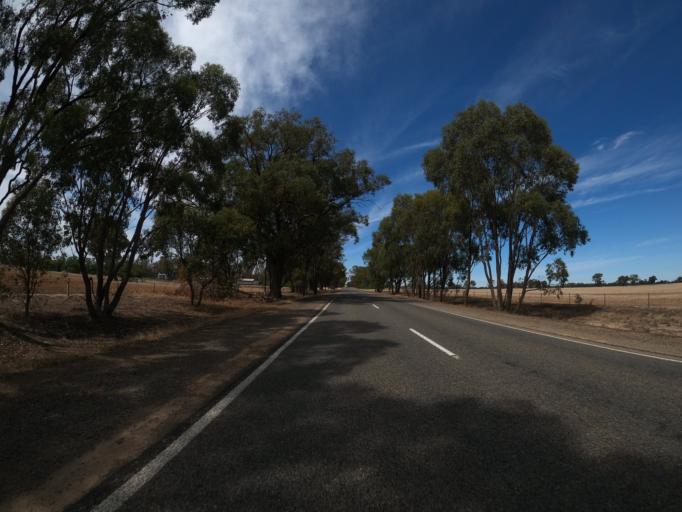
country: AU
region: Victoria
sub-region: Benalla
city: Benalla
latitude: -36.2904
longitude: 145.9523
